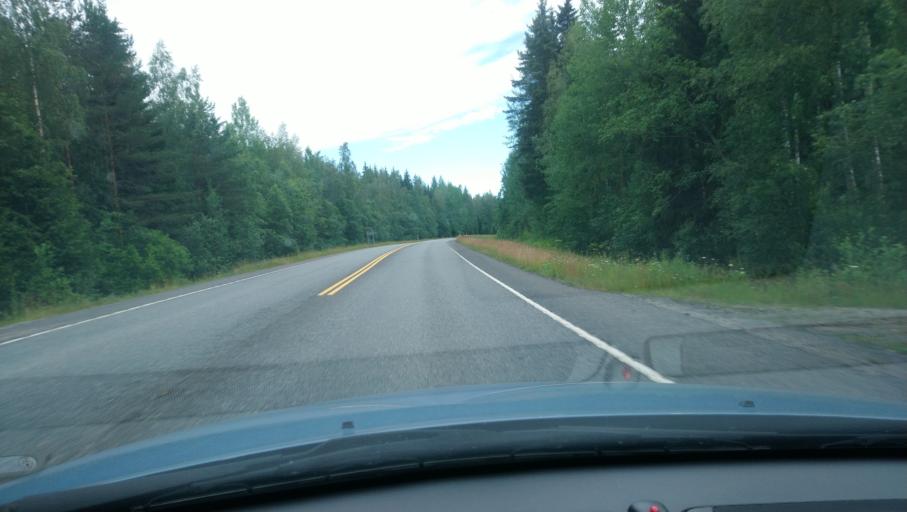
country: FI
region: Uusimaa
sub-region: Porvoo
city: Porvoo
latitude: 60.4349
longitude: 25.5748
